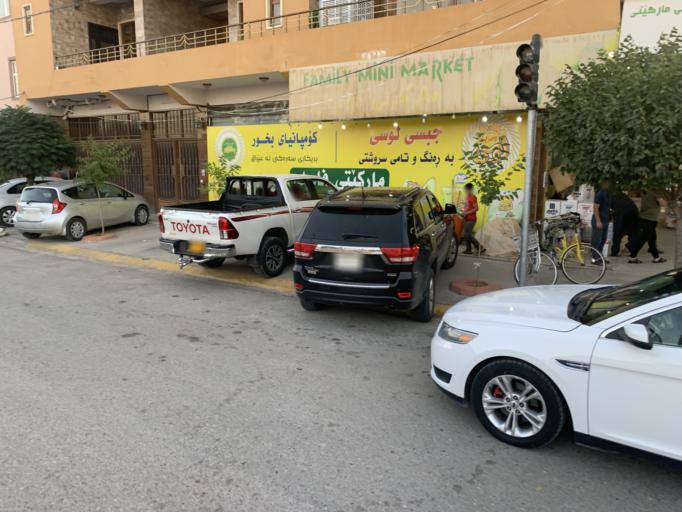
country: IQ
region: As Sulaymaniyah
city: Raniye
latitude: 36.2457
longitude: 44.8780
